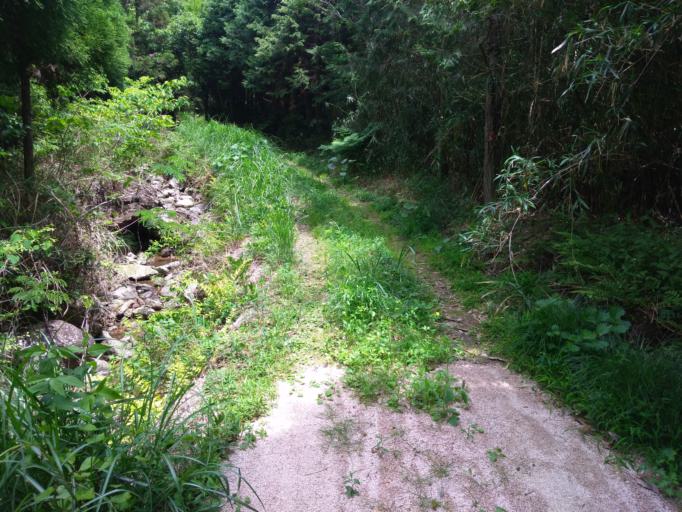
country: JP
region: Yamaguchi
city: Ogori-shimogo
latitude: 34.1188
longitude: 131.4591
